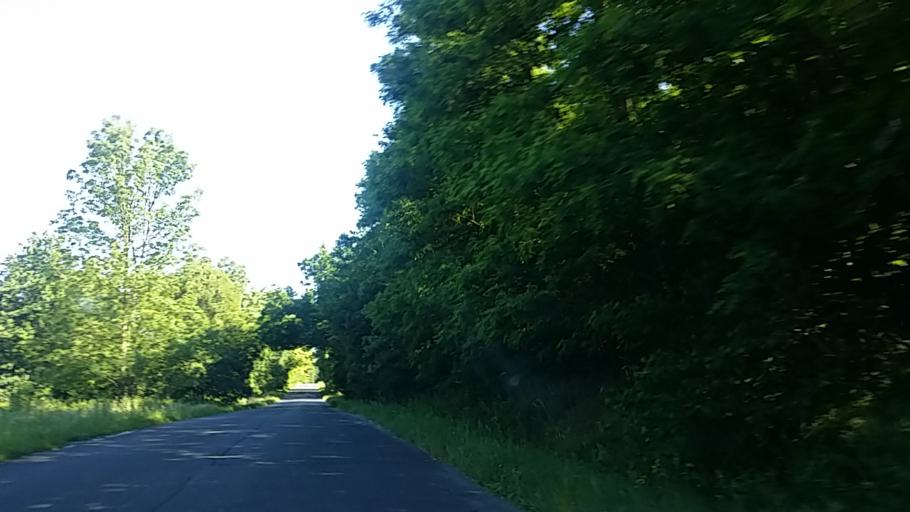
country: HU
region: Zala
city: Zalalovo
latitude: 46.8510
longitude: 16.5027
